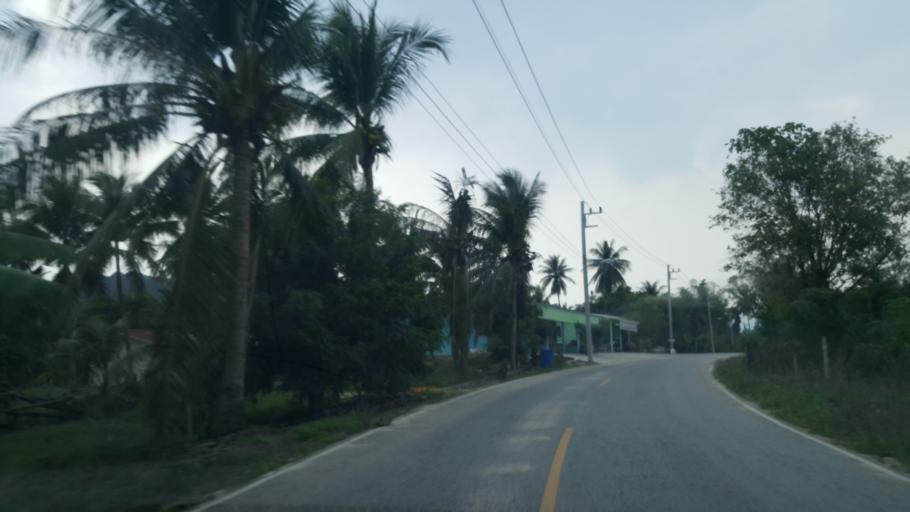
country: TH
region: Chon Buri
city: Ban Bueng
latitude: 13.2191
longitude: 101.0423
